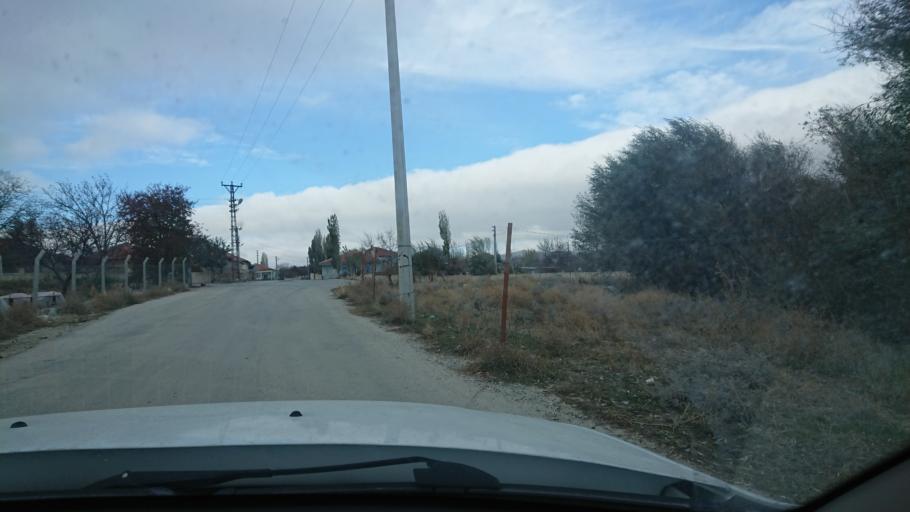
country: TR
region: Aksaray
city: Ortakoy
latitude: 38.7448
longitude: 34.0487
